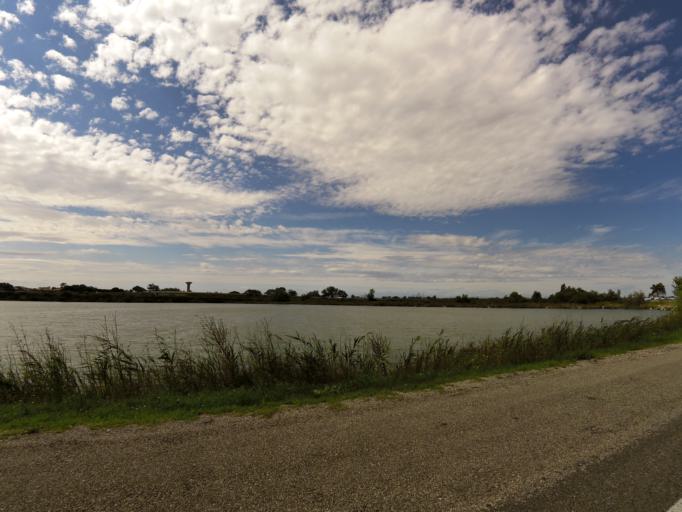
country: FR
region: Languedoc-Roussillon
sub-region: Departement du Gard
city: Le Grau-du-Roi
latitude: 43.5486
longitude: 4.1405
